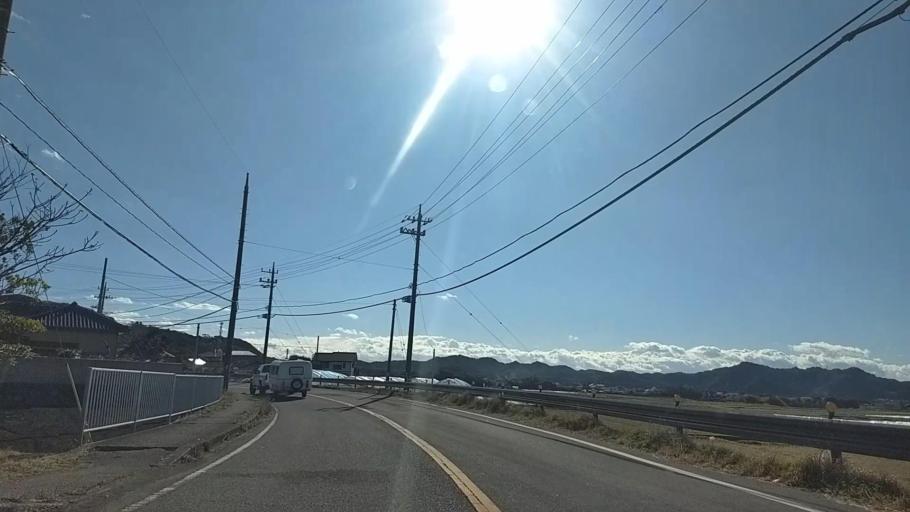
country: JP
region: Chiba
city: Tateyama
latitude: 34.9425
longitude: 139.8375
